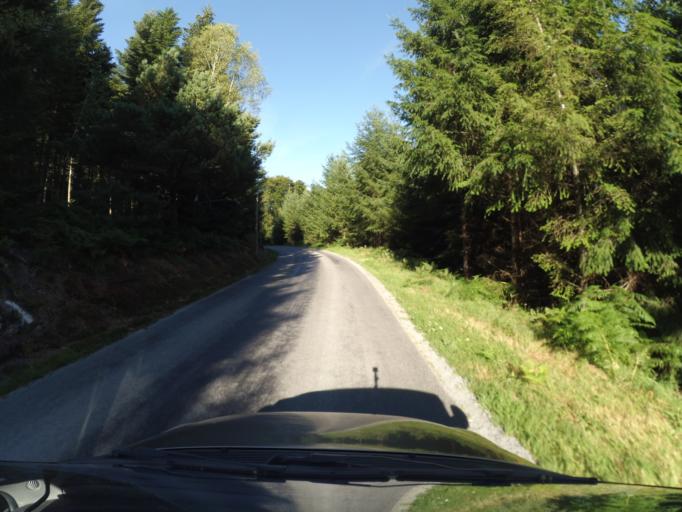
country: FR
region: Limousin
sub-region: Departement de la Creuse
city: Banize
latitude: 45.7842
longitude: 1.9796
